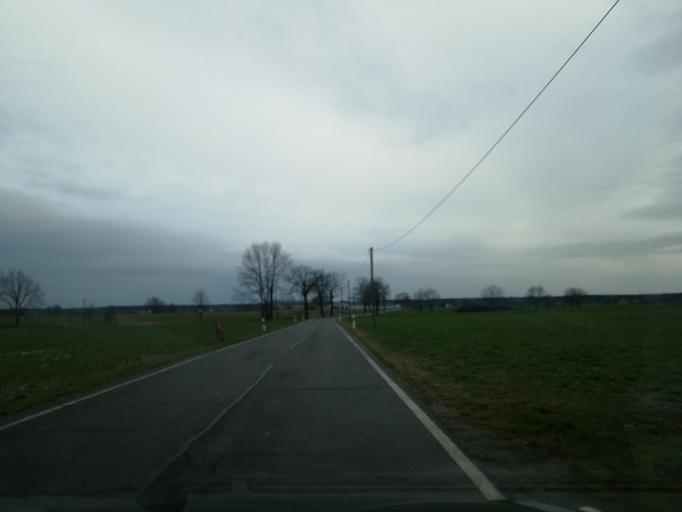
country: DE
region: Brandenburg
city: Calau
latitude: 51.7397
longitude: 14.0237
